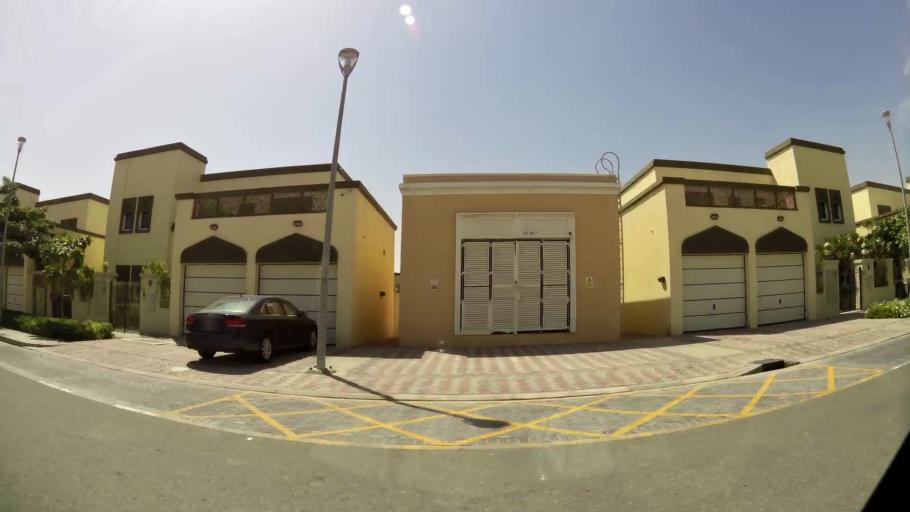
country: AE
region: Dubai
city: Dubai
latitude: 25.0497
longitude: 55.1483
